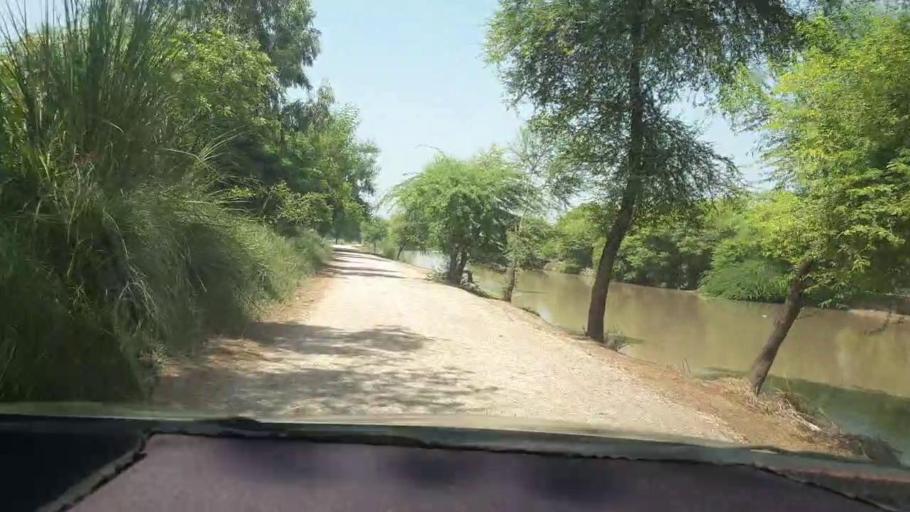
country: PK
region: Sindh
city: Kambar
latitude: 27.6075
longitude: 68.0835
